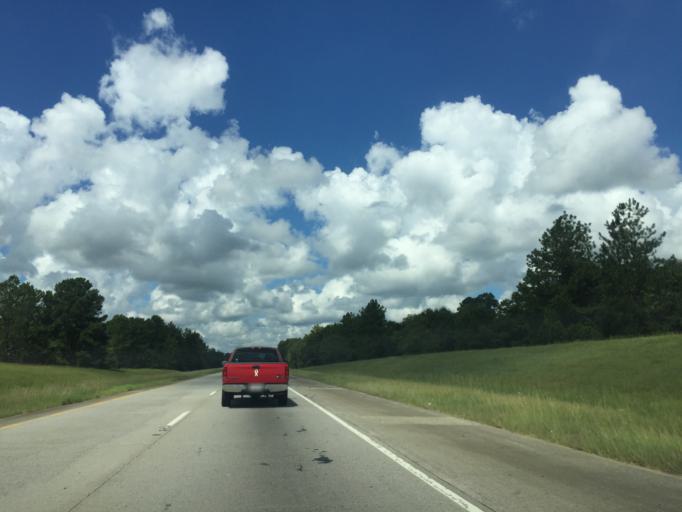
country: US
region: Georgia
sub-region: Candler County
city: Metter
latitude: 32.3801
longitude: -82.2025
